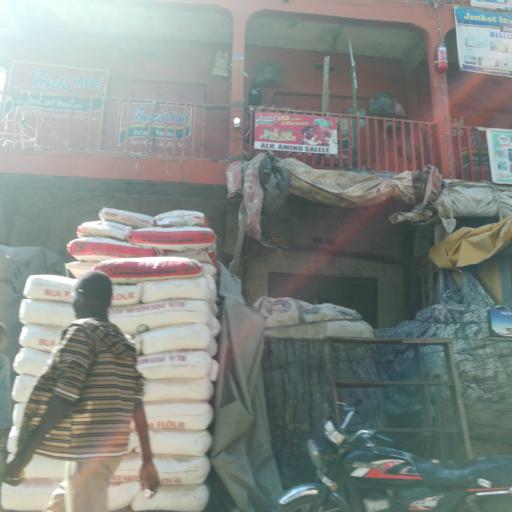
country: NG
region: Kano
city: Kano
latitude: 12.0103
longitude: 8.5369
